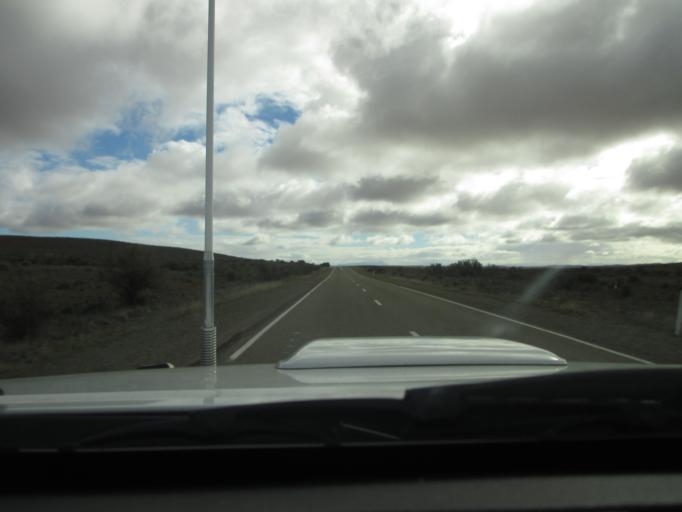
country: AU
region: South Australia
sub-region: Flinders Ranges
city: Quorn
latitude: -32.1343
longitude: 138.5135
